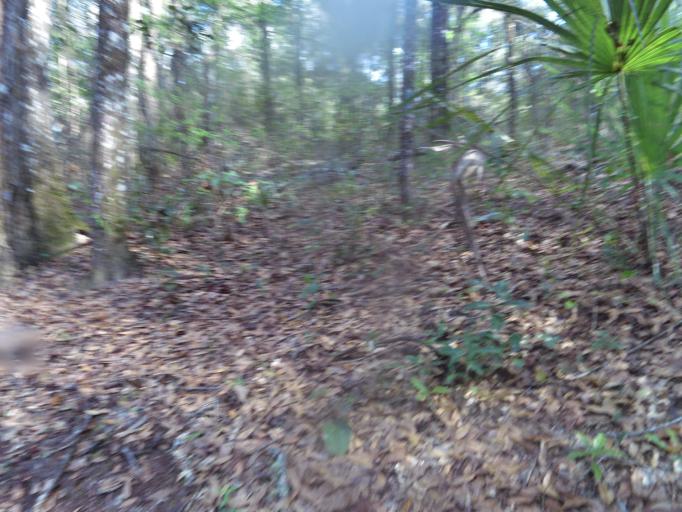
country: US
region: Florida
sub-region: Clay County
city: Middleburg
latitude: 30.1536
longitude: -81.9595
